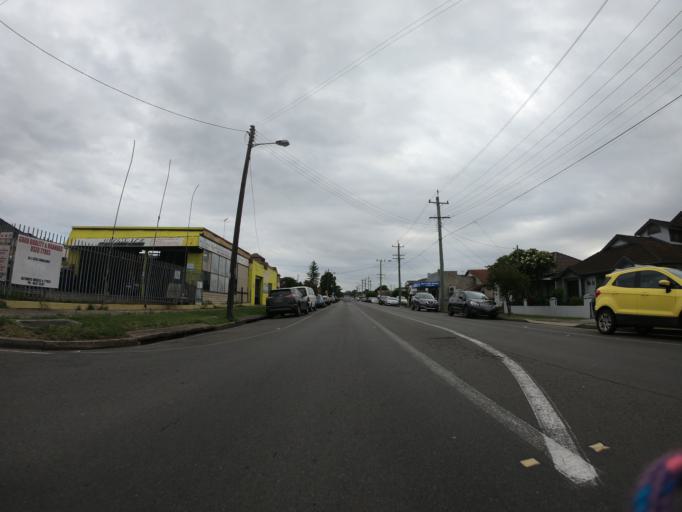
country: AU
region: New South Wales
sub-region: Parramatta
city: Granville
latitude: -33.8428
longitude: 151.0103
